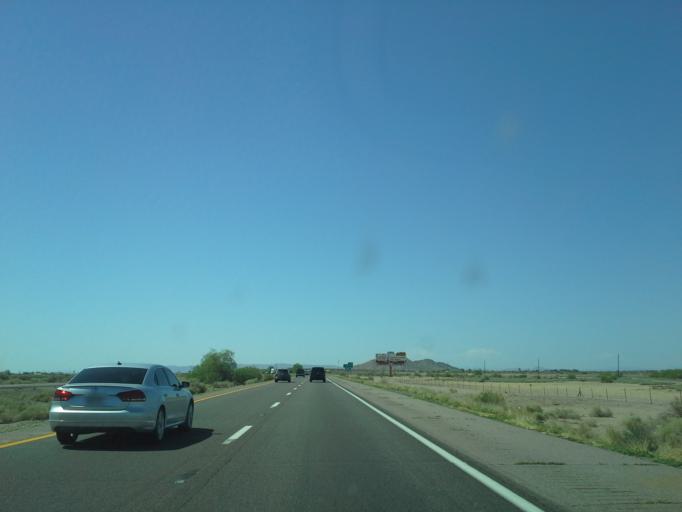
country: US
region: Arizona
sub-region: Pinal County
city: Casa Blanca
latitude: 33.1084
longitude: -111.8344
